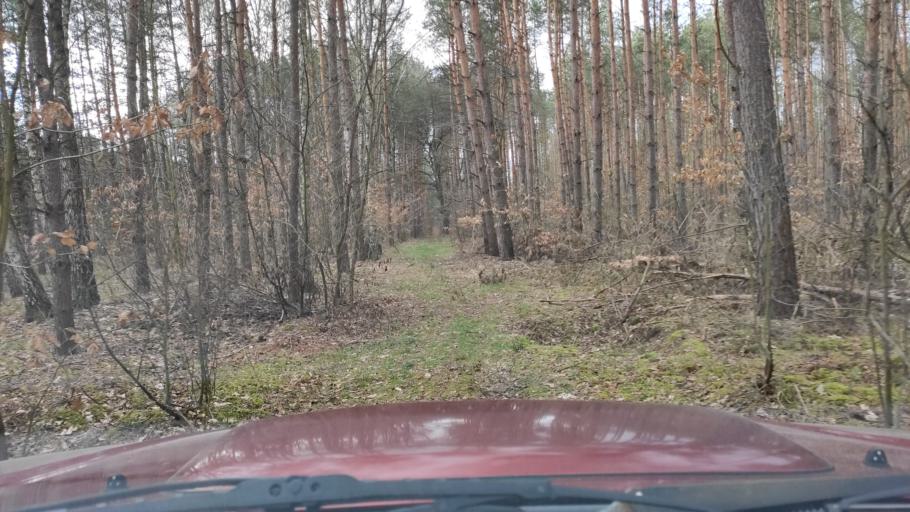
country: PL
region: Masovian Voivodeship
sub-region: Powiat kozienicki
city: Garbatka-Letnisko
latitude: 51.5122
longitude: 21.5724
